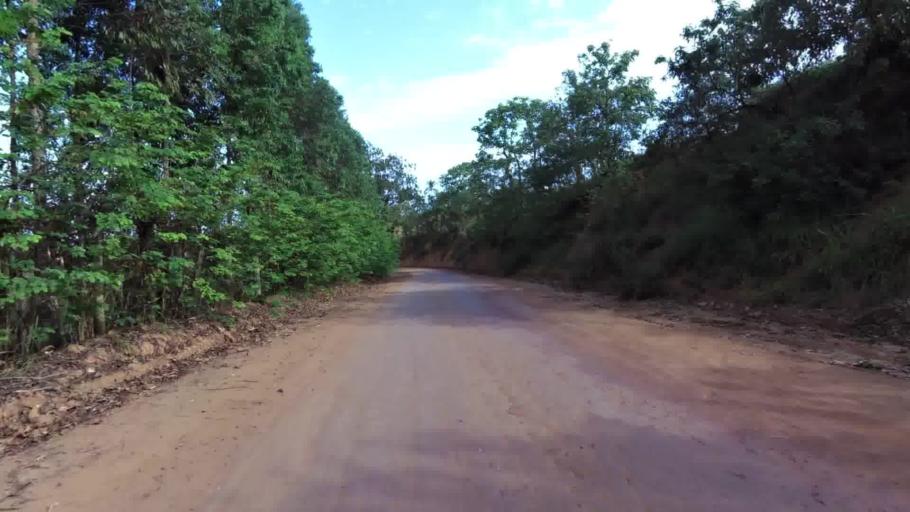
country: BR
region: Espirito Santo
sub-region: Piuma
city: Piuma
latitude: -20.8309
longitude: -40.7403
